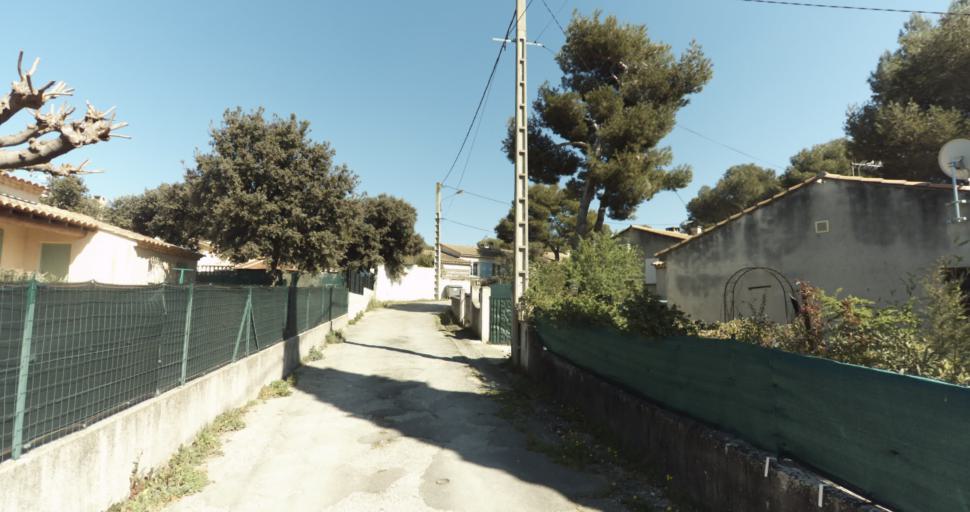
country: FR
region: Provence-Alpes-Cote d'Azur
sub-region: Departement des Bouches-du-Rhone
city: Pelissanne
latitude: 43.6380
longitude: 5.1572
